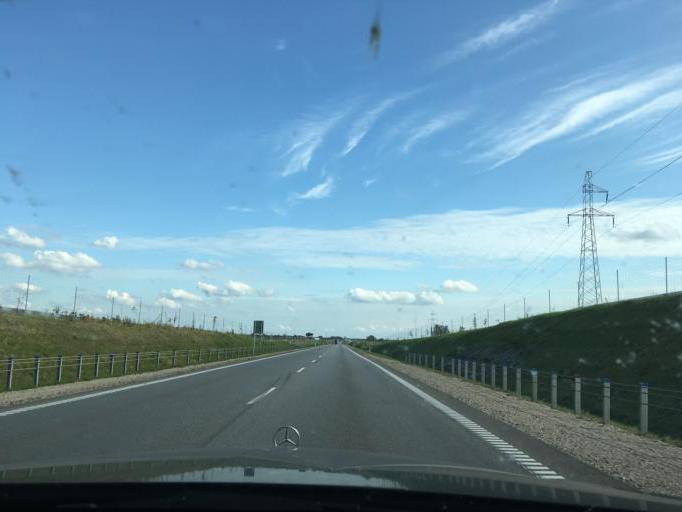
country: PL
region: Podlasie
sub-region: Powiat augustowski
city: Augustow
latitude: 53.8629
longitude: 22.9012
